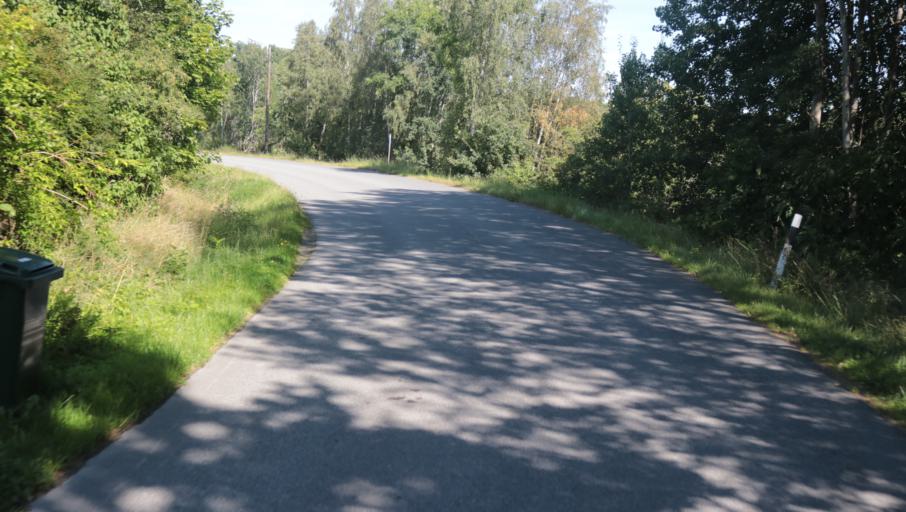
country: SE
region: Blekinge
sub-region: Karlshamns Kommun
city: Karlshamn
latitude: 56.1861
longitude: 14.8144
